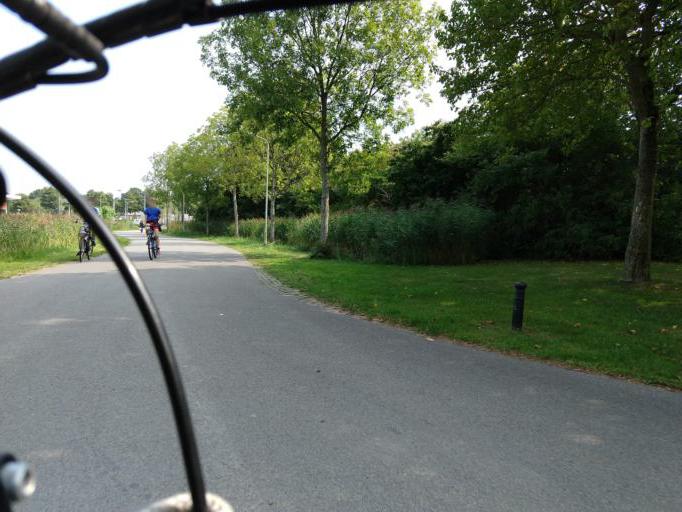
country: NL
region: Zeeland
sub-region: Gemeente Goes
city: Goes
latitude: 51.5121
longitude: 3.8866
